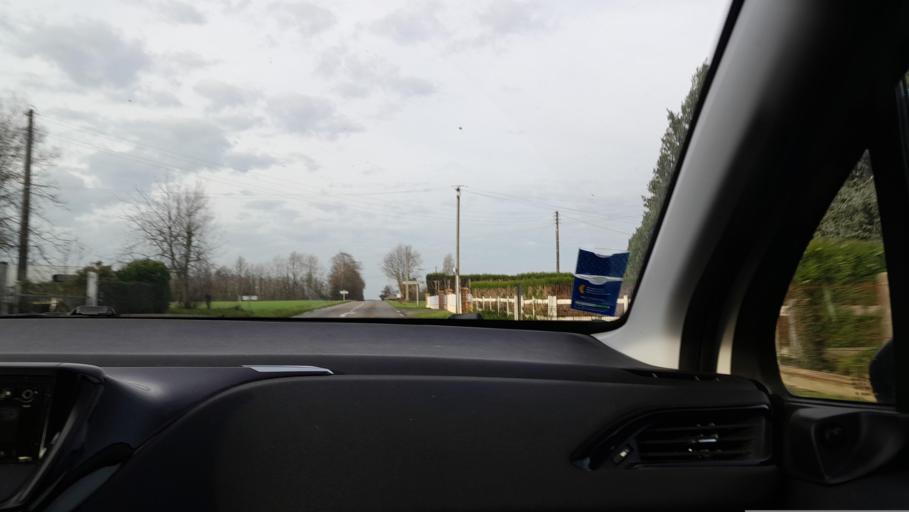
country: FR
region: Brittany
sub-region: Departement d'Ille-et-Vilaine
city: La Guerche-de-Bretagne
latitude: 47.9016
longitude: -1.1448
